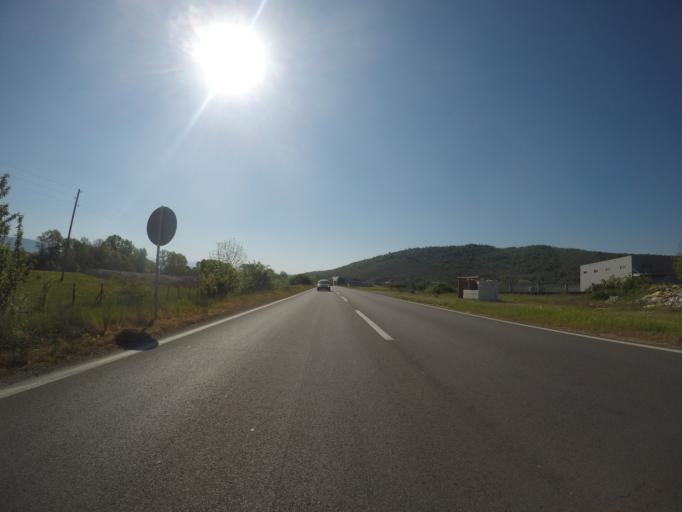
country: ME
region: Danilovgrad
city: Danilovgrad
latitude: 42.5123
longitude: 19.1280
